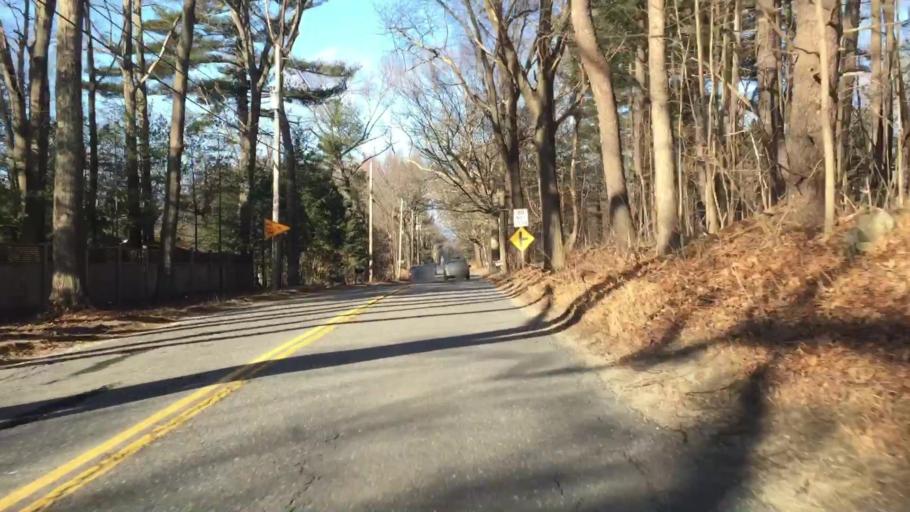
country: US
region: Massachusetts
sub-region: Worcester County
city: West Boylston
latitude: 42.4099
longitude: -71.8000
